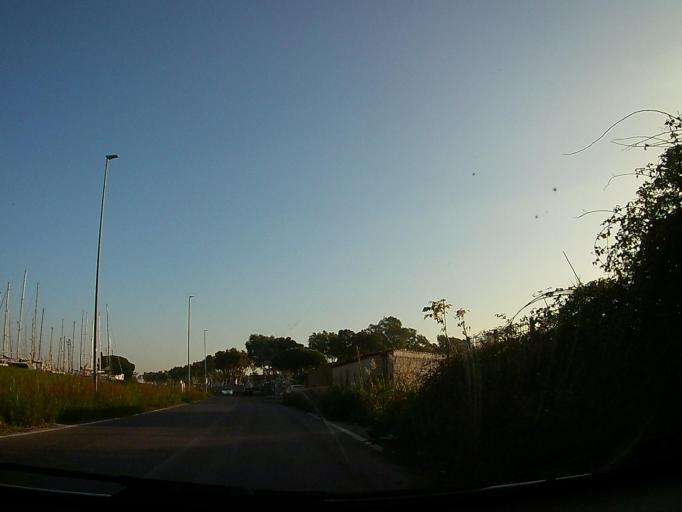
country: IT
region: Latium
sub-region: Citta metropolitana di Roma Capitale
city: Lido di Ostia
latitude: 41.7462
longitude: 12.2682
